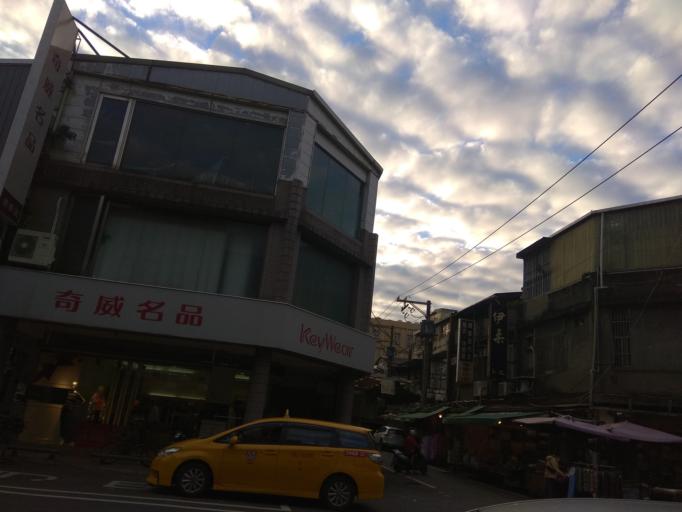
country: TW
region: Taiwan
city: Taoyuan City
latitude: 24.9920
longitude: 121.3077
